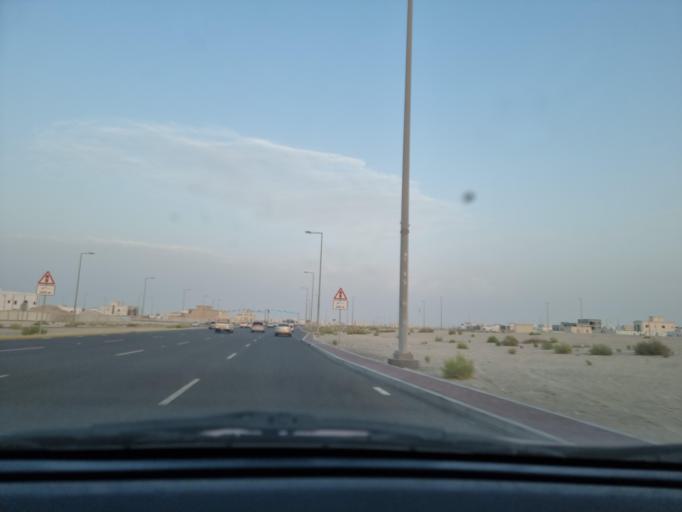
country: AE
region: Abu Dhabi
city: Abu Dhabi
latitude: 24.3716
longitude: 54.7445
